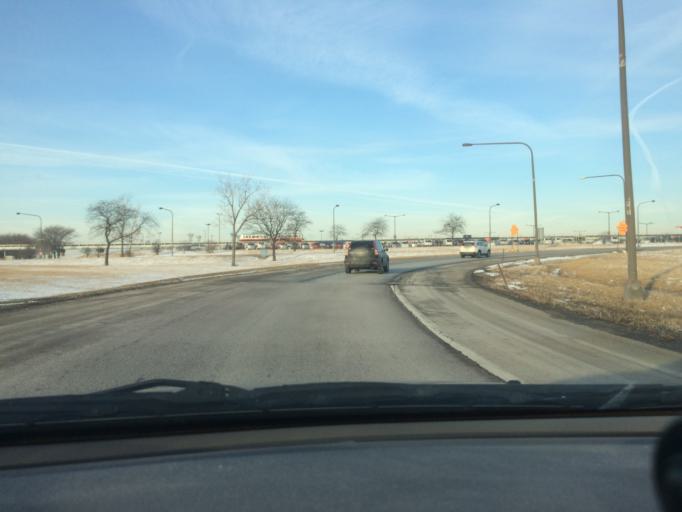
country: US
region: Illinois
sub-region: Cook County
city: Rosemont
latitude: 41.9808
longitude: -87.8800
